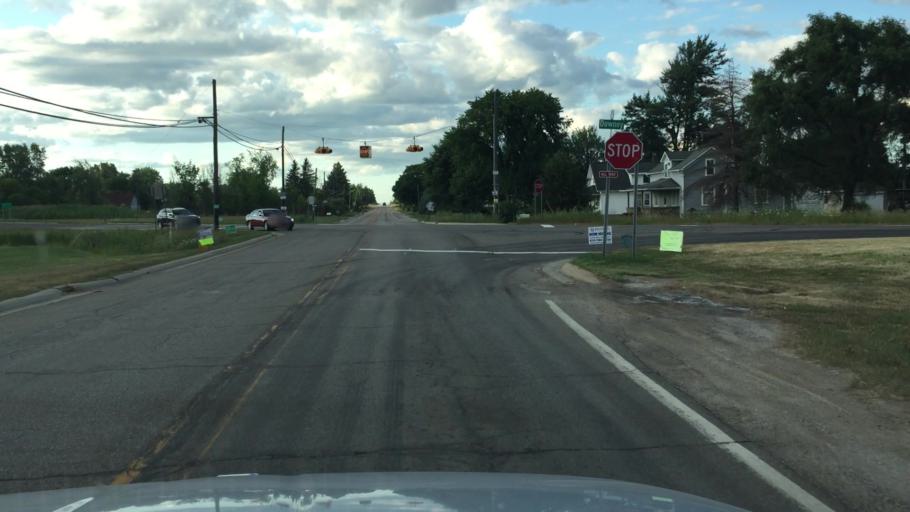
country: US
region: Michigan
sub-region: Saint Clair County
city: Capac
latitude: 43.0219
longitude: -82.9287
